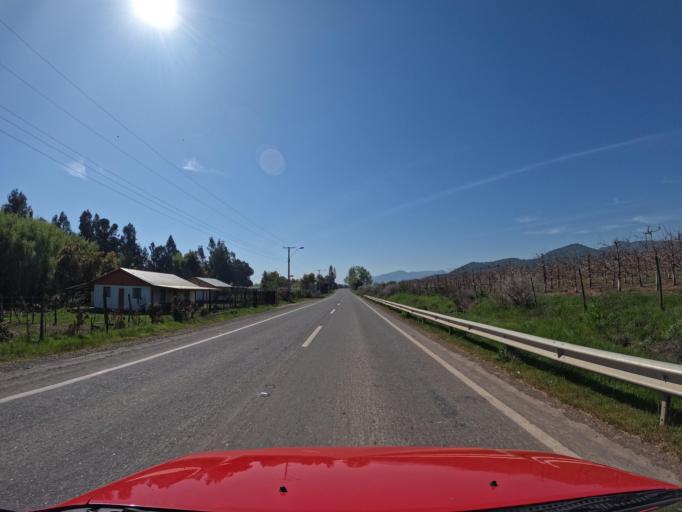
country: CL
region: Maule
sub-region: Provincia de Curico
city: Molina
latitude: -35.0542
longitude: -71.4820
